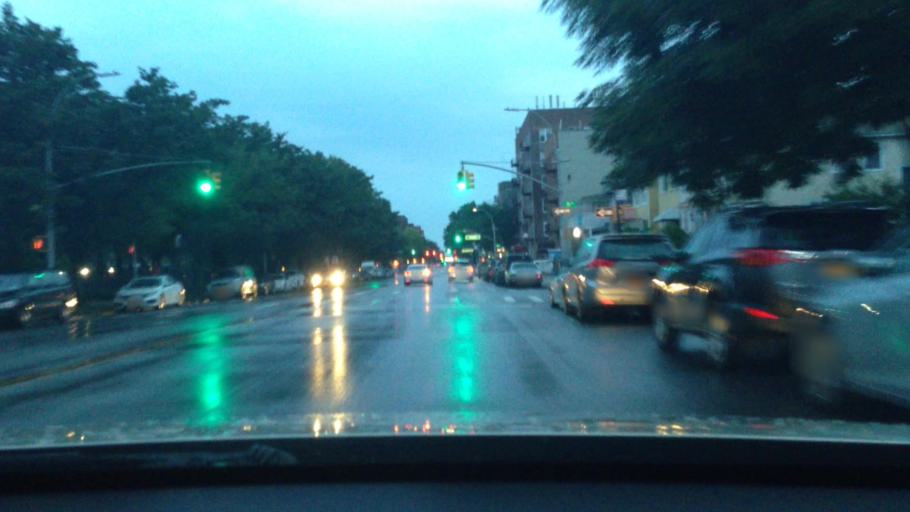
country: US
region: New York
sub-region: Kings County
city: Bensonhurst
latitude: 40.6096
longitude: -73.9859
